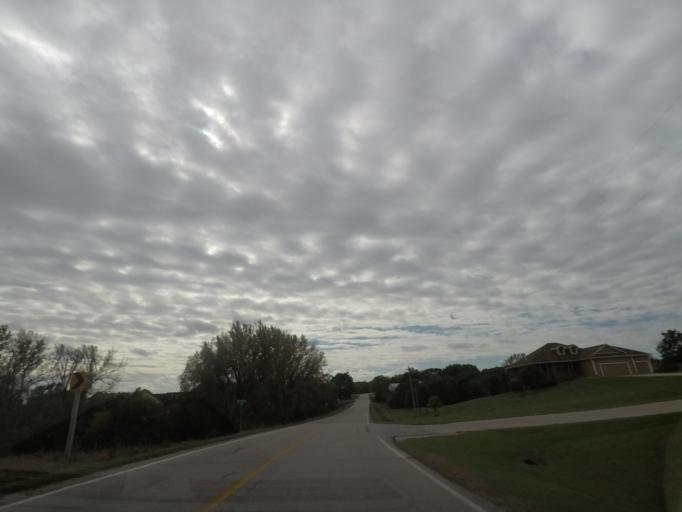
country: US
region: Iowa
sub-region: Story County
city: Huxley
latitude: 41.8379
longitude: -93.5316
